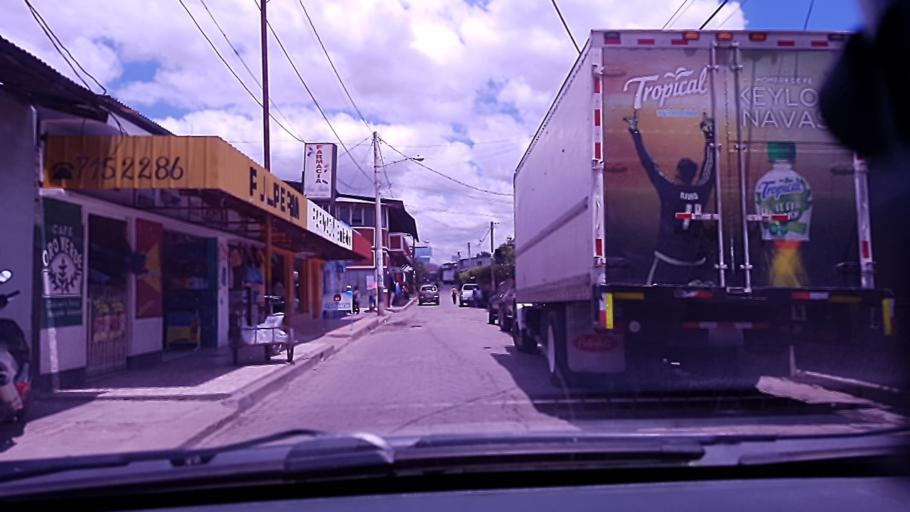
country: NI
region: Esteli
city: Condega
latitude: 13.3614
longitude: -86.3986
